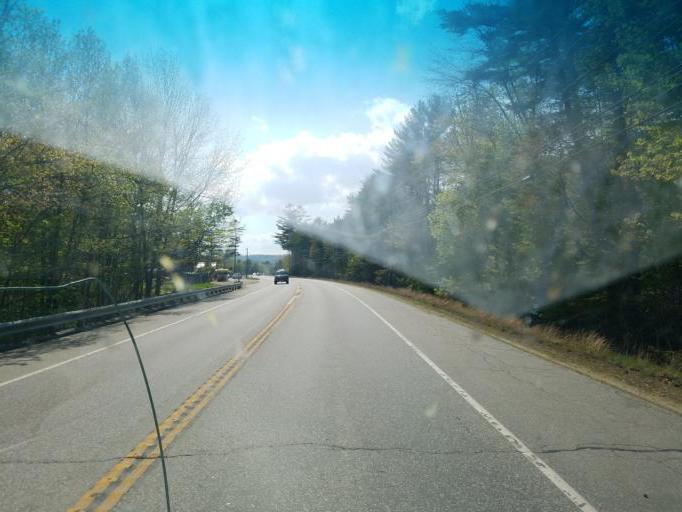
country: US
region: Maine
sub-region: Oxford County
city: Dixfield
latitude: 44.5313
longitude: -70.4634
